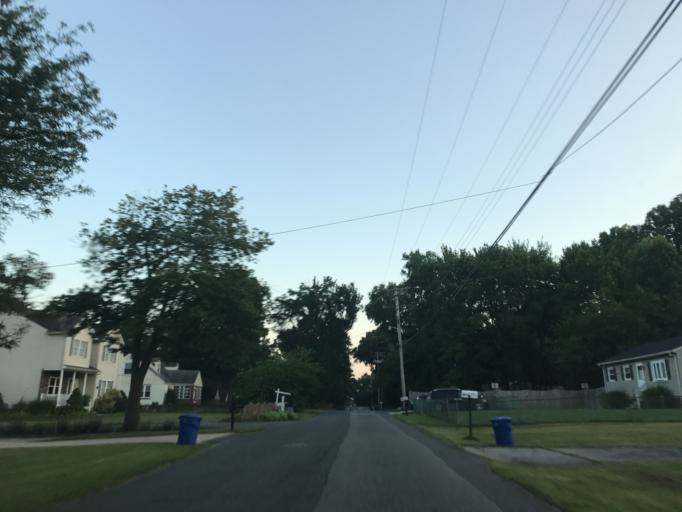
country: US
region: Maryland
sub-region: Baltimore County
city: Middle River
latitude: 39.3093
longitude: -76.4378
